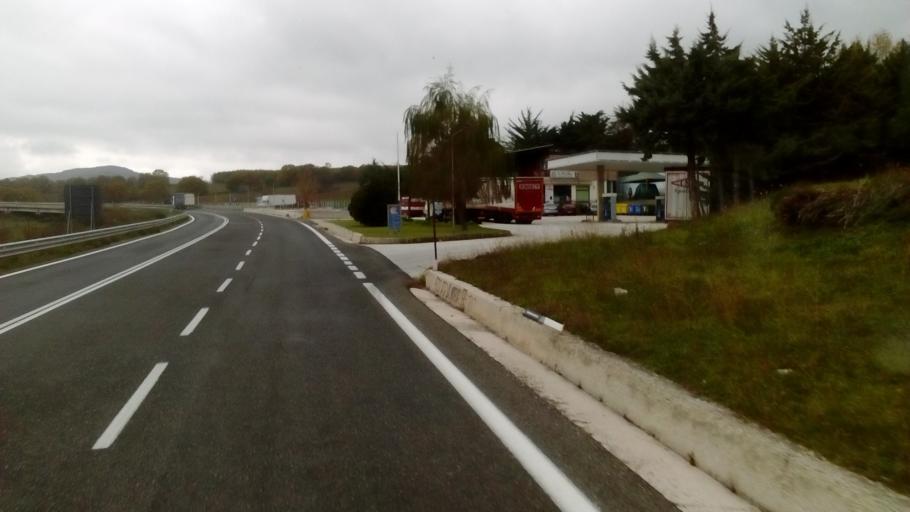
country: IT
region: Molise
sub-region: Provincia di Isernia
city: Bagnoli del Trigno
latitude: 41.7192
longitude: 14.4270
